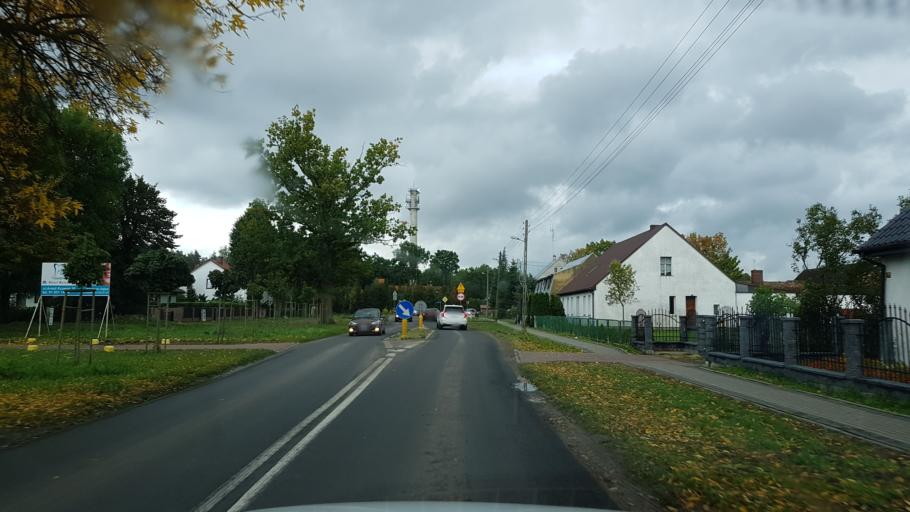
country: PL
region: West Pomeranian Voivodeship
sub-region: Powiat goleniowski
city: Goleniow
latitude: 53.4610
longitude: 14.7724
